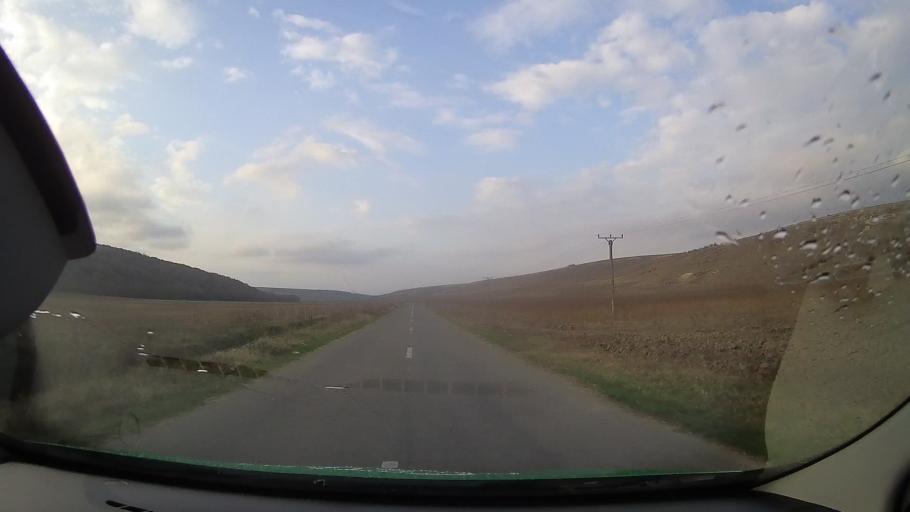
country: RO
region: Constanta
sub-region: Comuna Dobromir
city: Dobromir
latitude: 44.0236
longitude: 27.8688
